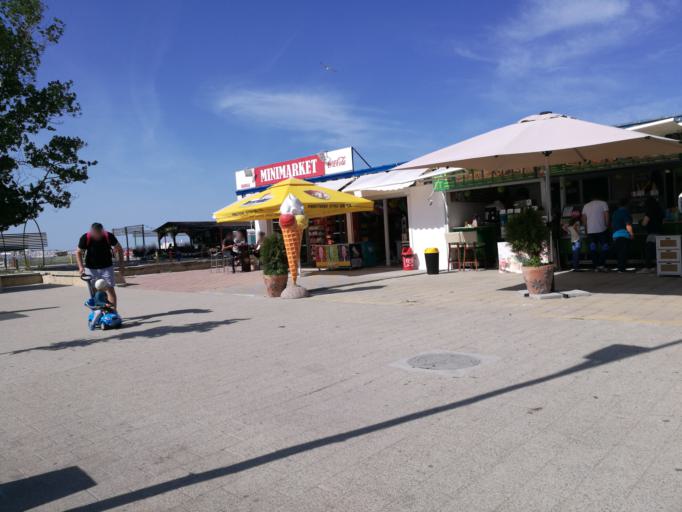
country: RO
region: Constanta
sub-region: Municipiul Constanta
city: Palazu Mare
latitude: 44.2272
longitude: 28.6298
